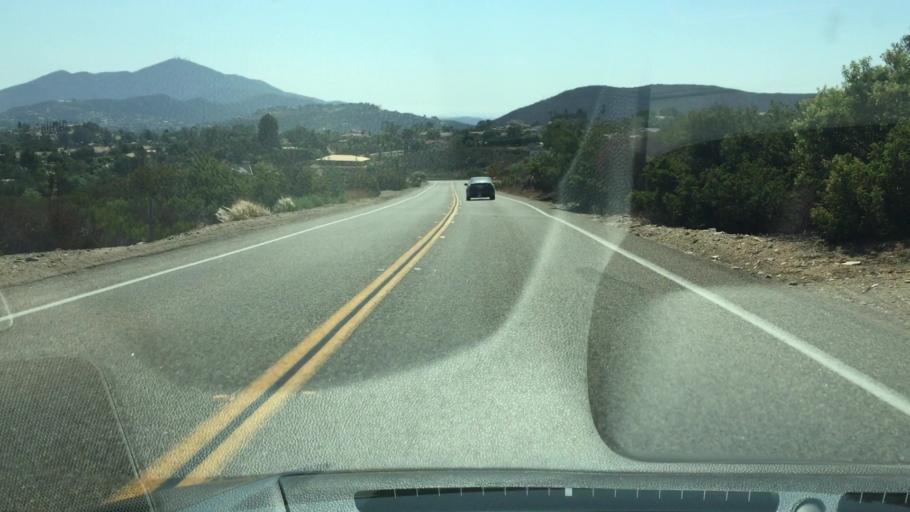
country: US
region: California
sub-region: San Diego County
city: Jamul
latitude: 32.7356
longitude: -116.8466
